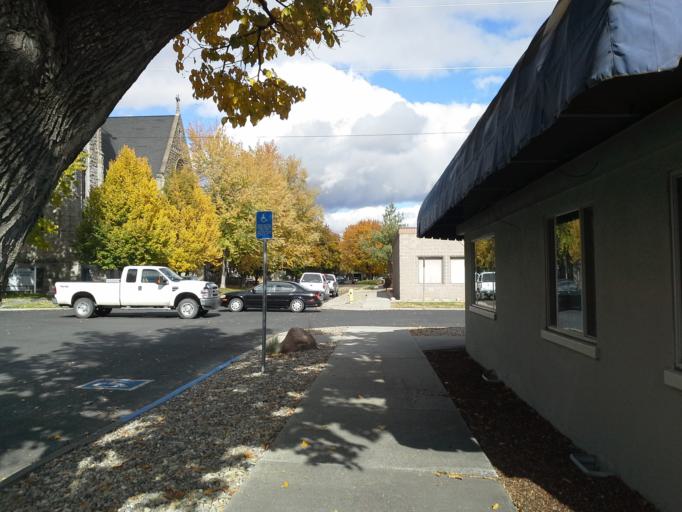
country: US
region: Oregon
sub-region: Baker County
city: Baker City
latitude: 44.7789
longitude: -117.8307
